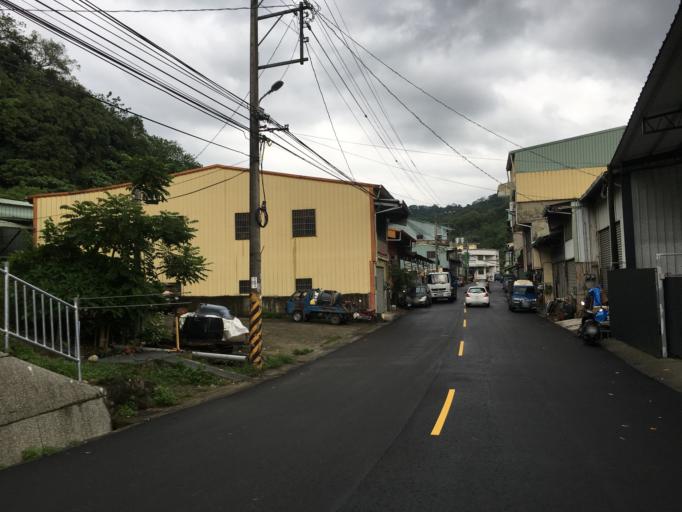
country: TW
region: Taiwan
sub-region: Taichung City
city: Taichung
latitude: 24.0634
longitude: 120.7375
